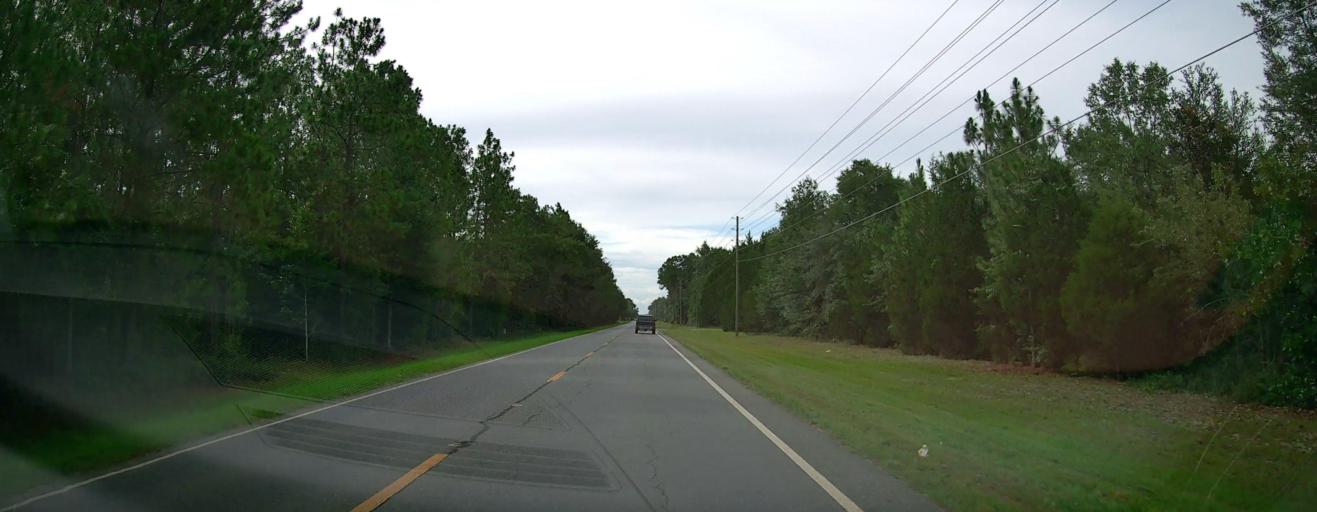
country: US
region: Georgia
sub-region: Wayne County
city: Jesup
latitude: 31.6472
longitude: -81.9084
